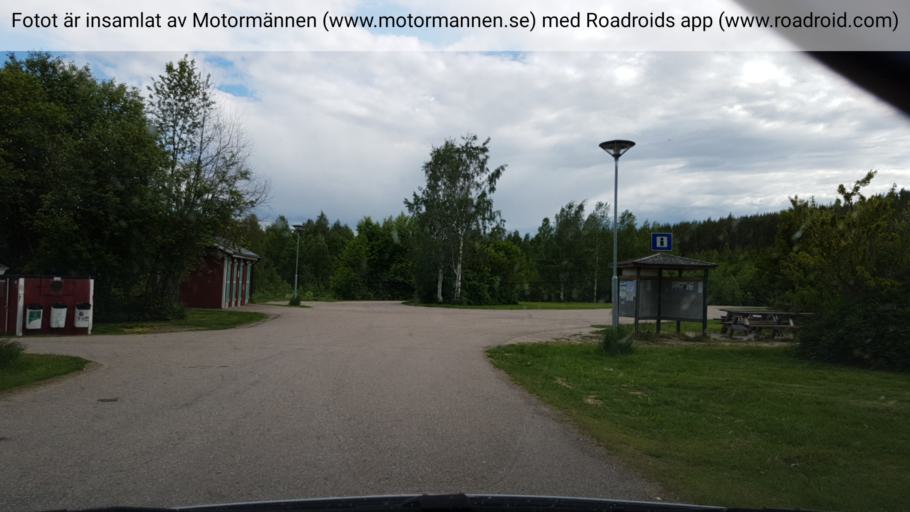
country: SE
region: Norrbotten
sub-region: Overkalix Kommun
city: OEverkalix
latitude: 66.6506
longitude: 22.1838
